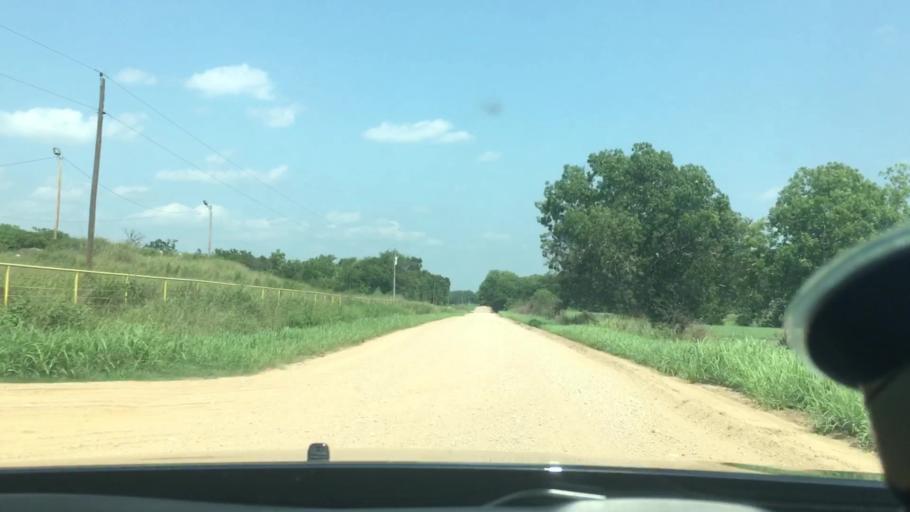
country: US
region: Oklahoma
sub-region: Coal County
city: Coalgate
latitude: 34.4295
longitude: -96.4568
